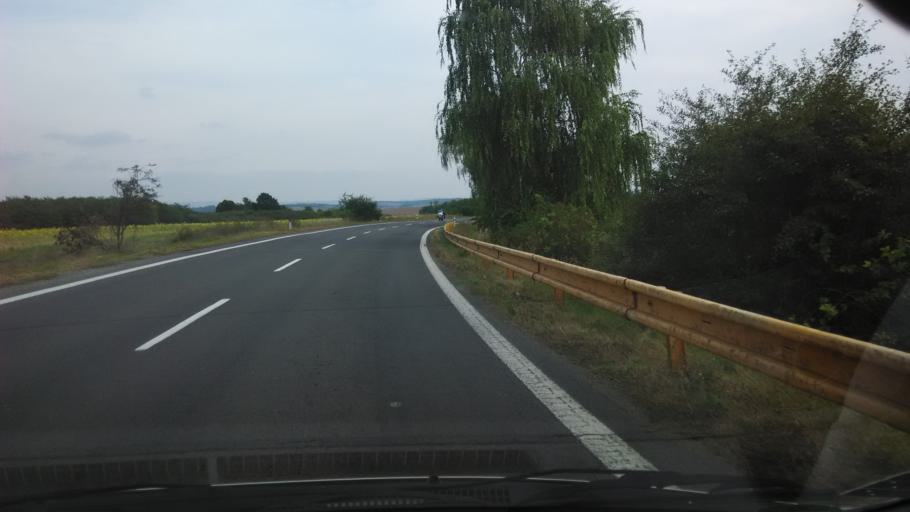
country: SK
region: Nitriansky
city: Zeliezovce
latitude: 48.1266
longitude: 18.7319
